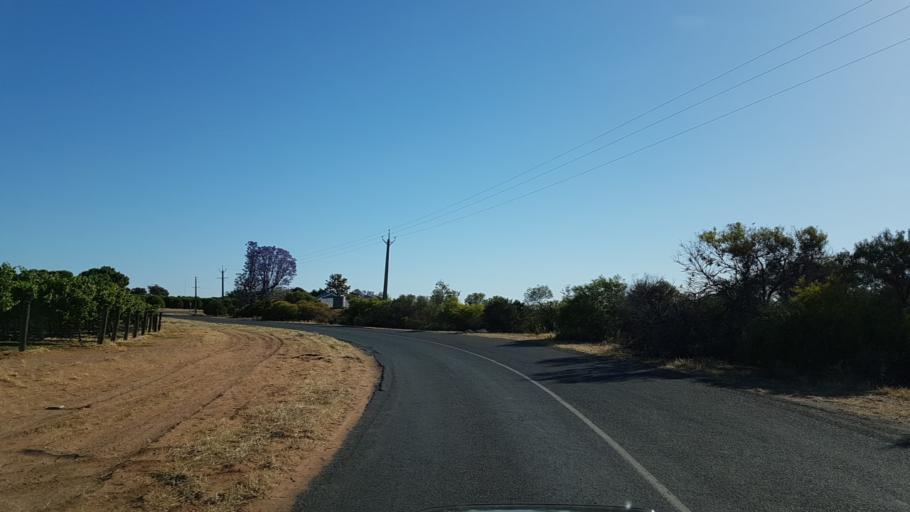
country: AU
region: South Australia
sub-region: Loxton Waikerie
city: Waikerie
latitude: -34.1726
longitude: 140.0310
